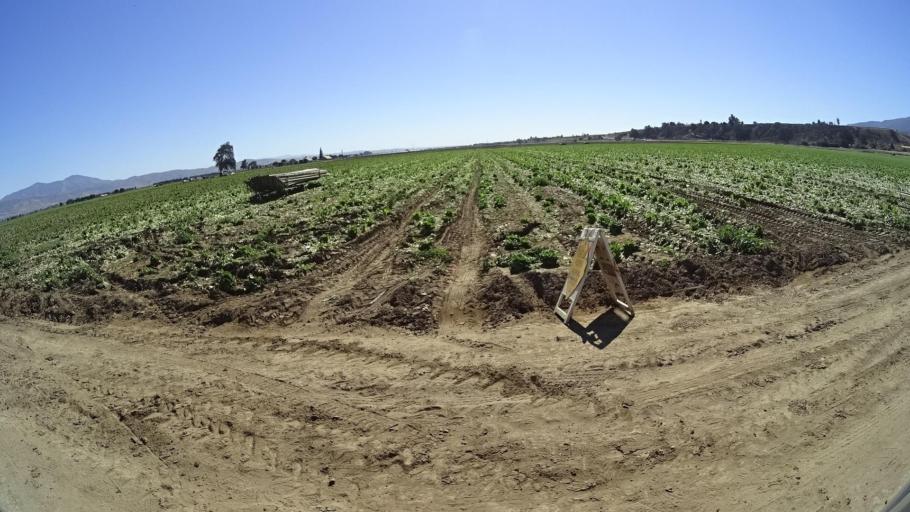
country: US
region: California
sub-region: Monterey County
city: Soledad
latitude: 36.3885
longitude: -121.3502
